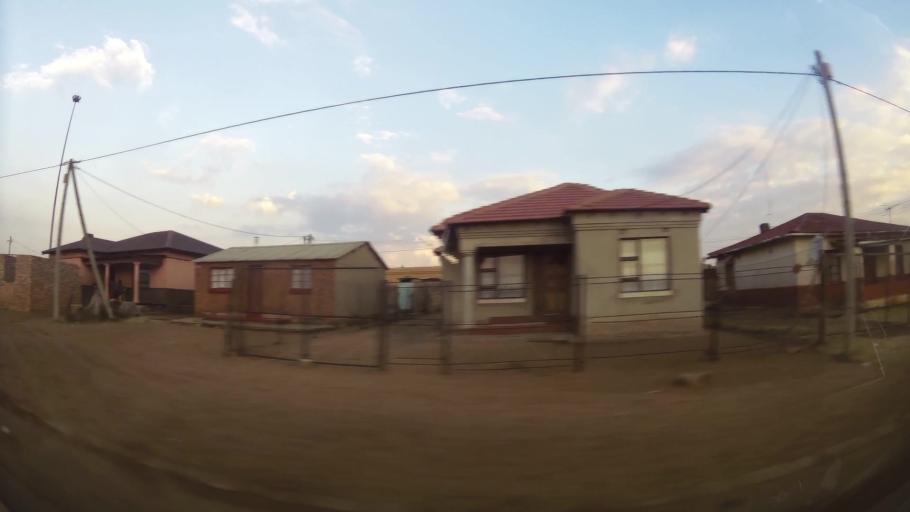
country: ZA
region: Gauteng
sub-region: City of Johannesburg Metropolitan Municipality
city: Orange Farm
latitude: -26.5479
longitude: 27.8797
